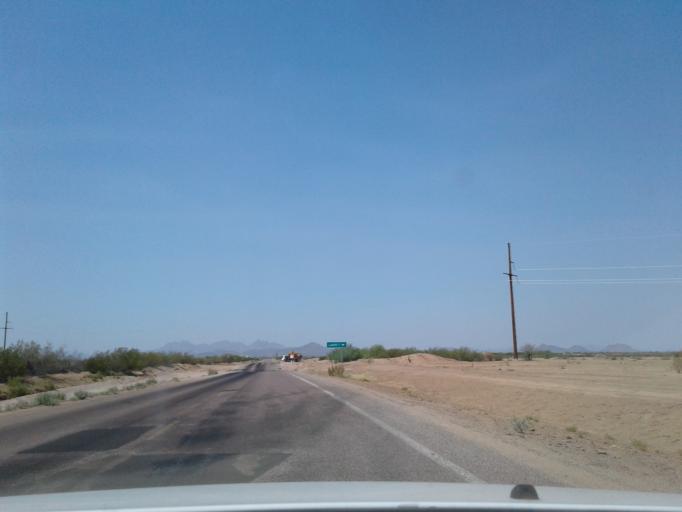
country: US
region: Arizona
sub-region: Pima County
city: Avra Valley
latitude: 32.6020
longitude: -111.3263
